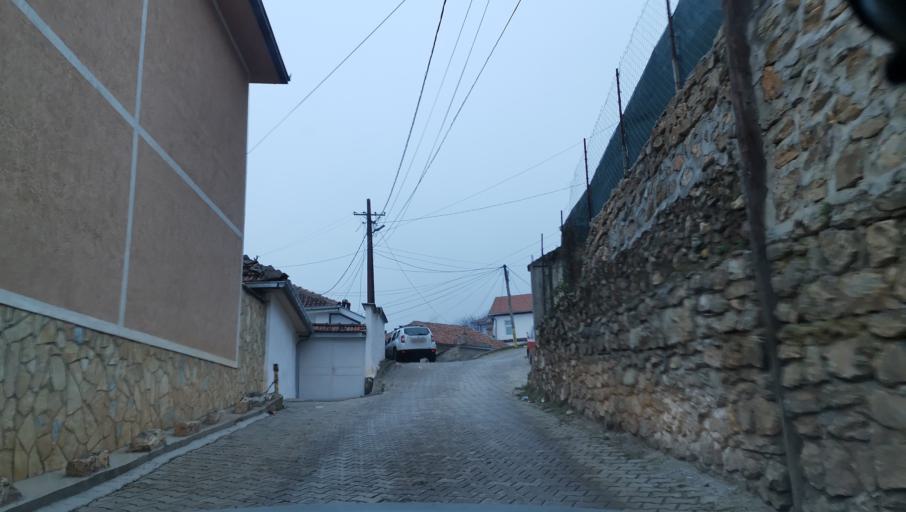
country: MK
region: Debar
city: Debar
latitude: 41.5259
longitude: 20.5279
